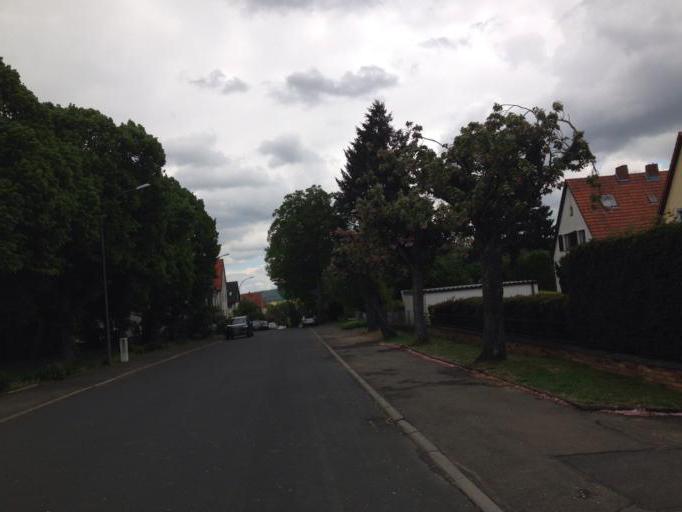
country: DE
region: Hesse
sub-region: Regierungsbezirk Giessen
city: Alsfeld
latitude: 50.7539
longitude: 9.2581
